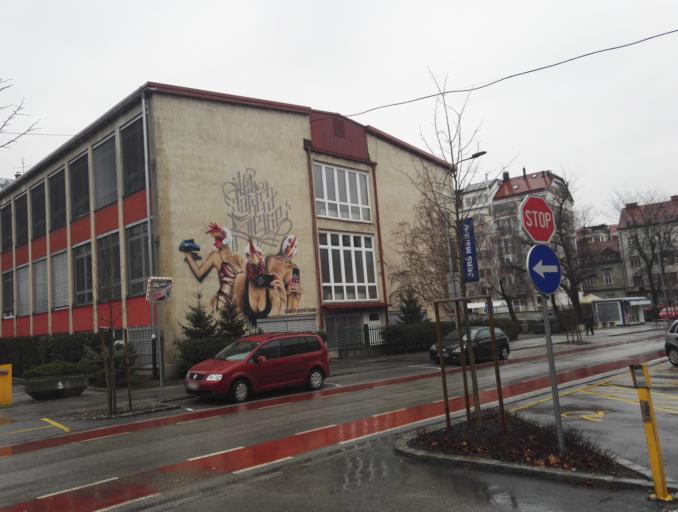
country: SI
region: Maribor
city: Maribor
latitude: 46.5593
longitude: 15.6404
